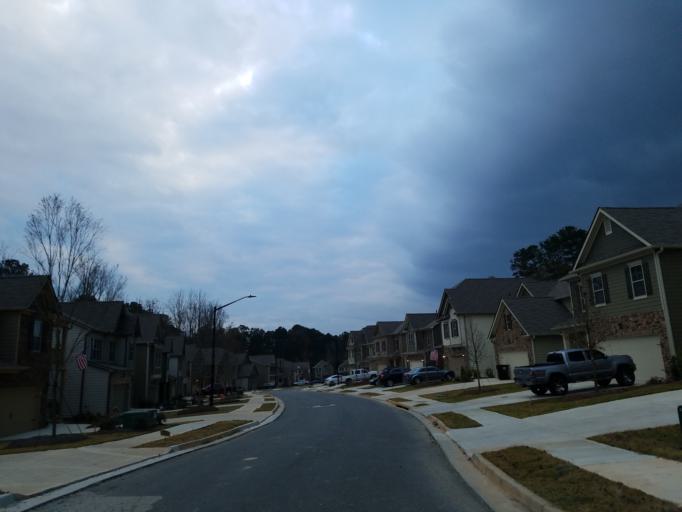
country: US
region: Georgia
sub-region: Cobb County
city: Acworth
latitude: 34.0920
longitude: -84.6283
